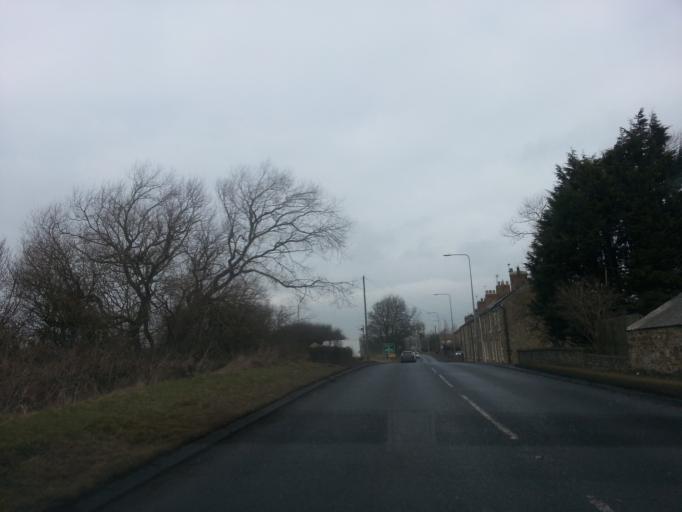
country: GB
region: England
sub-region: County Durham
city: High Etherley
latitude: 54.6234
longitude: -1.7098
